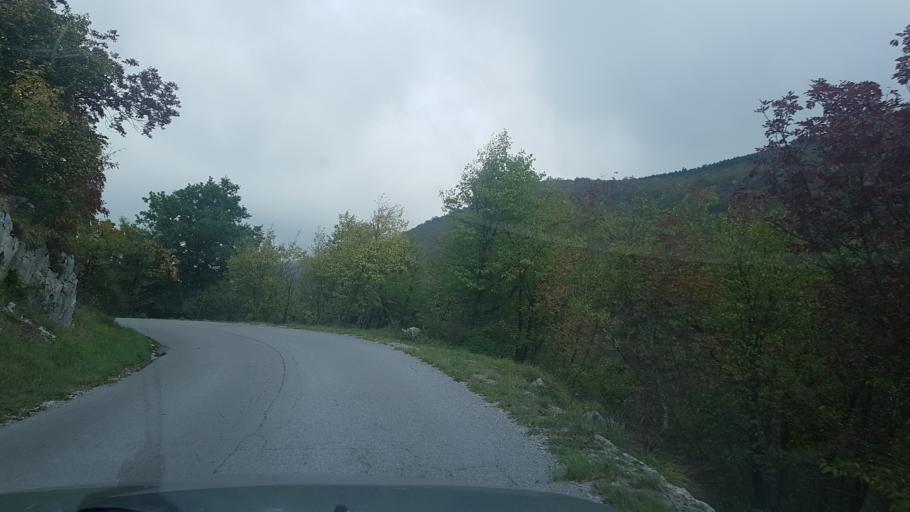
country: SI
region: Hrpelje-Kozina
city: Kozina
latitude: 45.5129
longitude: 13.9620
